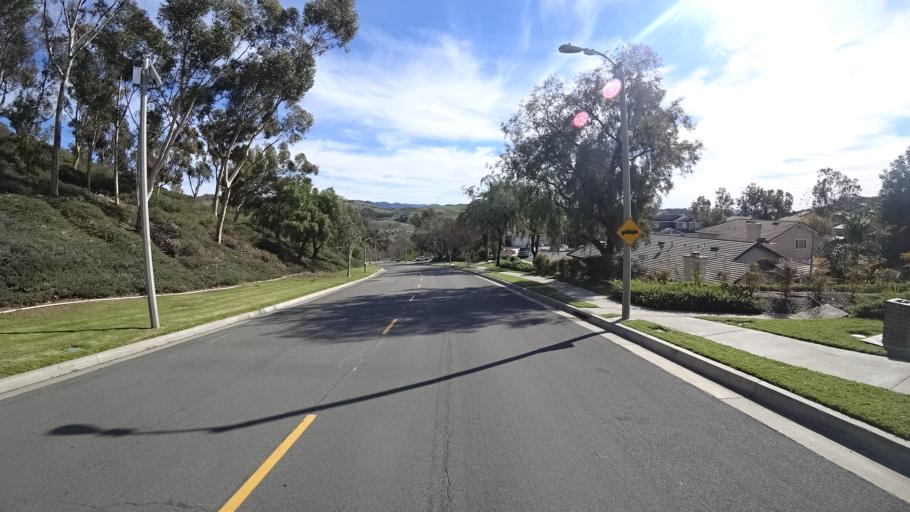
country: US
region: California
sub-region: Orange County
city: Portola Hills
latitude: 33.6844
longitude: -117.6264
